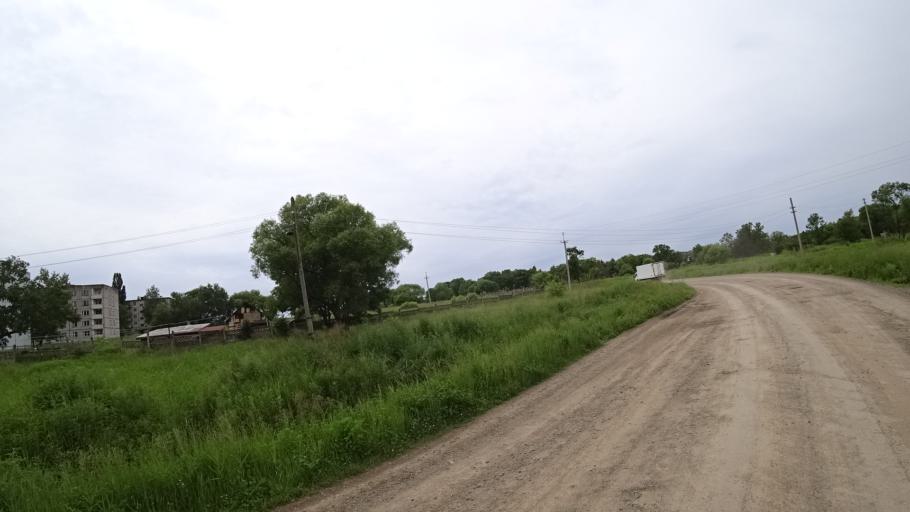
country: RU
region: Primorskiy
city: Novosysoyevka
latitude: 44.2023
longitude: 133.3159
